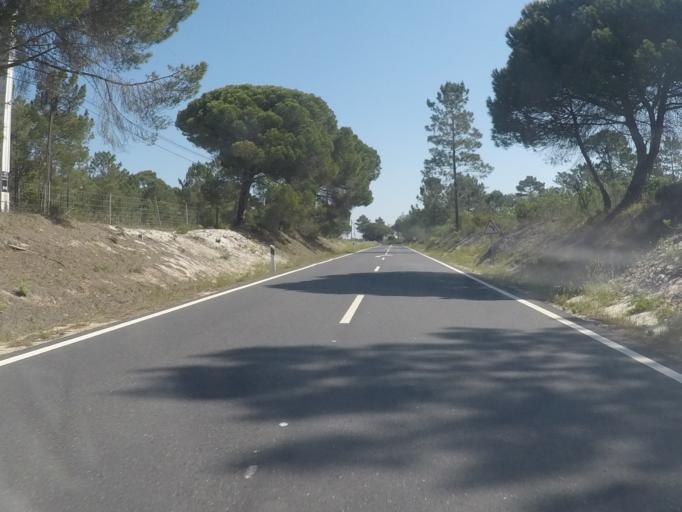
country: PT
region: Setubal
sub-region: Grandola
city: Grandola
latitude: 38.2613
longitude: -8.7321
